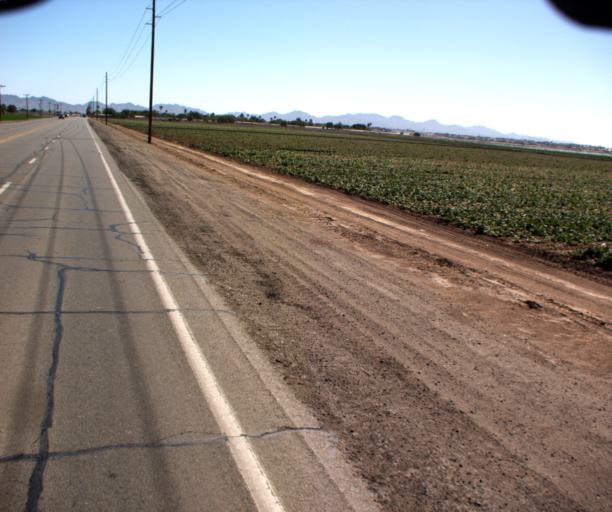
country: US
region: Arizona
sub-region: Yuma County
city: Yuma
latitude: 32.6989
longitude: -114.5539
